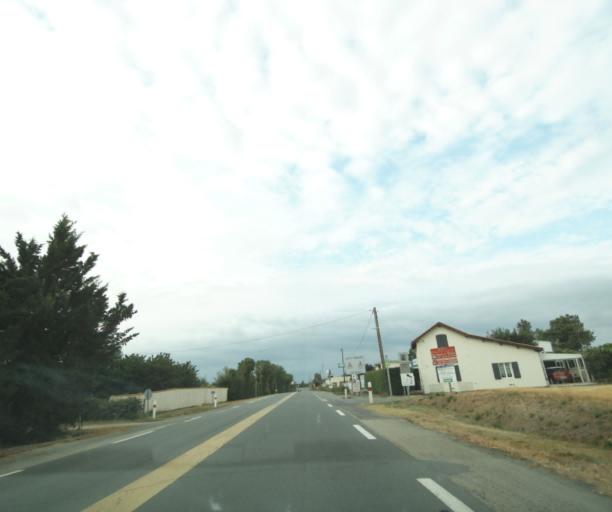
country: FR
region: Poitou-Charentes
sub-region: Departement de la Charente-Maritime
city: Marans
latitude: 46.2986
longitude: -0.9907
